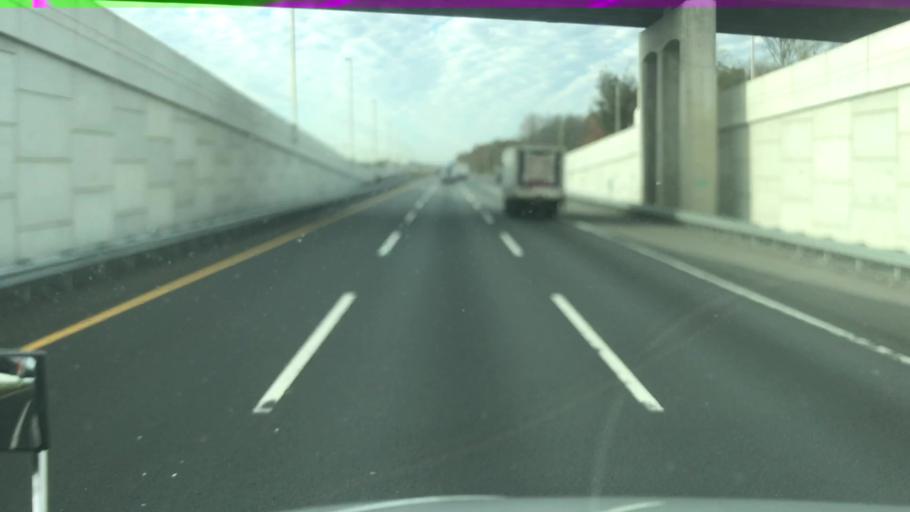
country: US
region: New Jersey
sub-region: Monmouth County
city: Allentown
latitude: 40.1912
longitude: -74.6055
